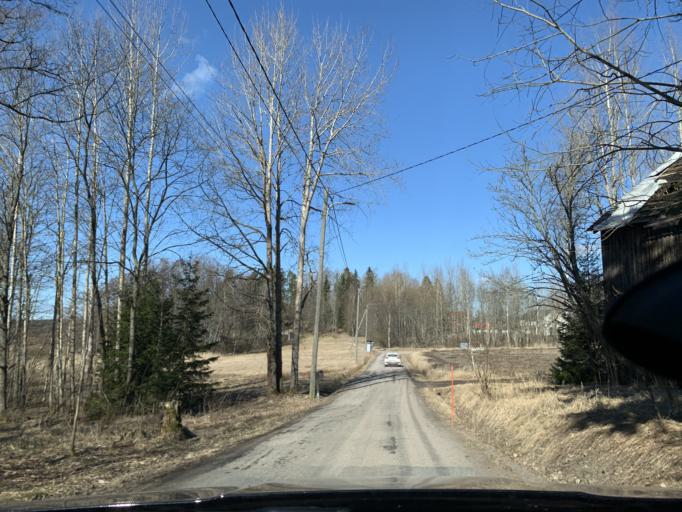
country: FI
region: Uusimaa
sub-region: Helsinki
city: Espoo
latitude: 60.1728
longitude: 24.5824
